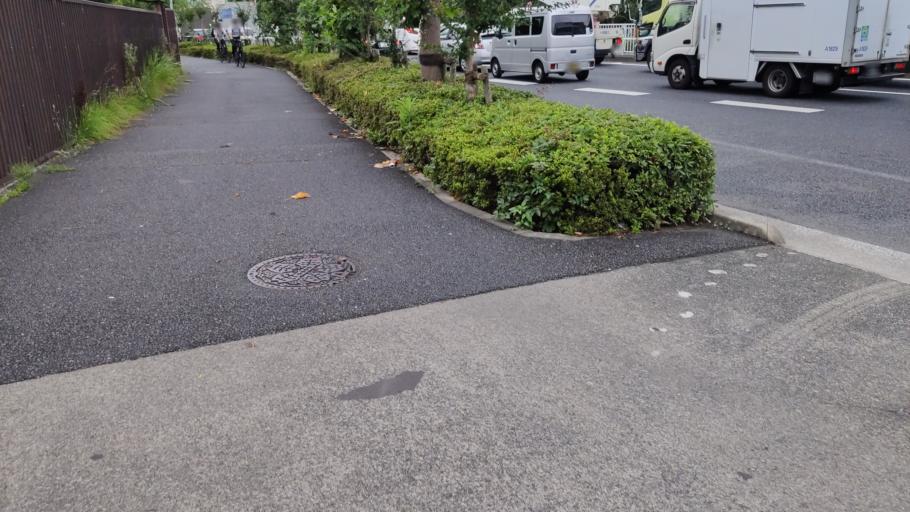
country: JP
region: Tokyo
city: Urayasu
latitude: 35.6659
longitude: 139.8398
